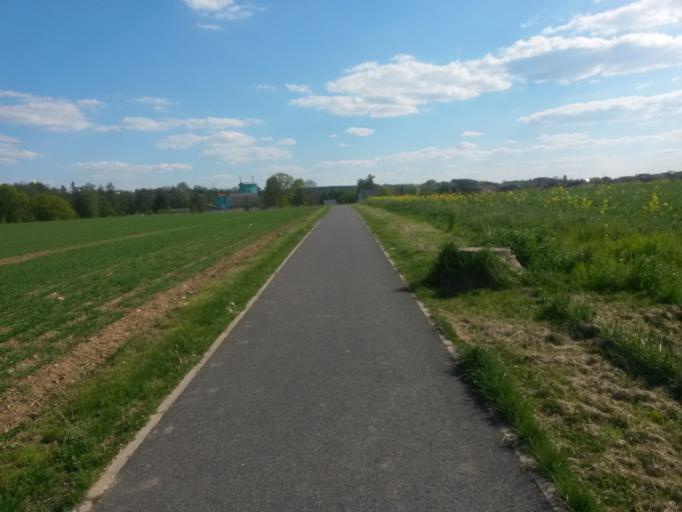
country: CZ
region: Central Bohemia
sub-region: Okres Praha-Zapad
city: Pruhonice
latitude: 49.9753
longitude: 14.5427
